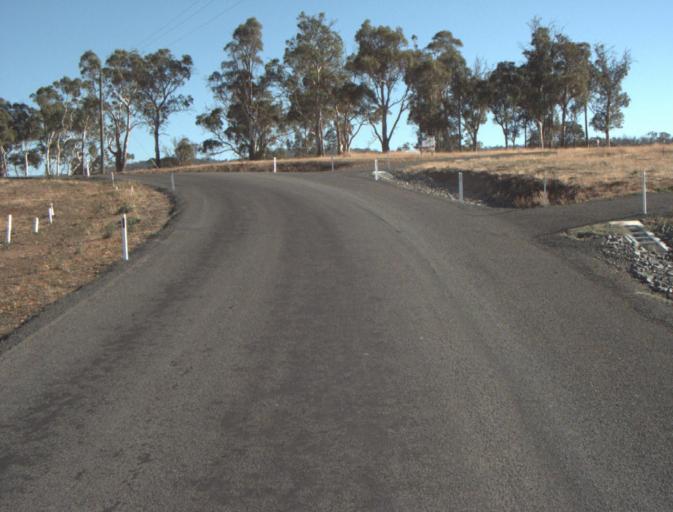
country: AU
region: Tasmania
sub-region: Launceston
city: Newstead
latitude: -41.4391
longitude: 147.2315
